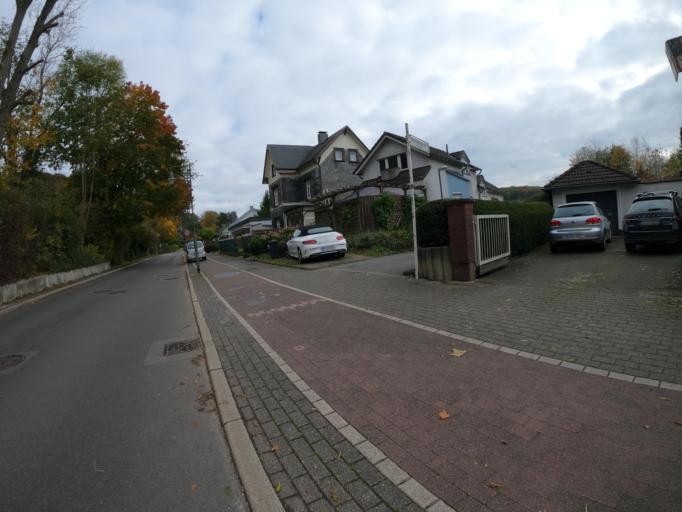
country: DE
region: North Rhine-Westphalia
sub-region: Regierungsbezirk Dusseldorf
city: Wuppertal
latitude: 51.2625
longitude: 7.1104
